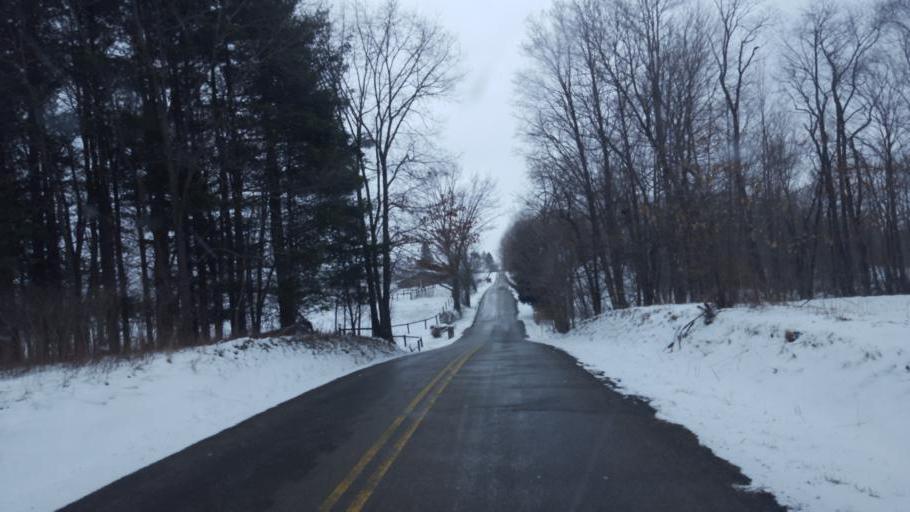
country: US
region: Pennsylvania
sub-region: Crawford County
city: Cochranton
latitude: 41.4237
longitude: -80.0458
